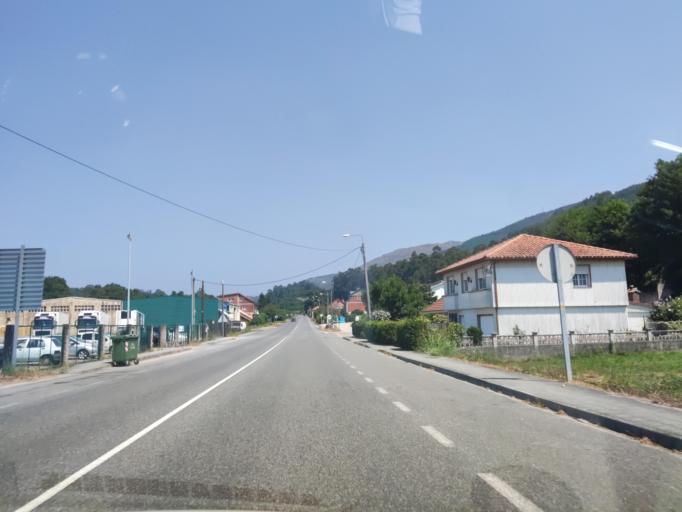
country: ES
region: Galicia
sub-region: Provincia de Pontevedra
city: Porrino
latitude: 42.2049
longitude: -8.6016
